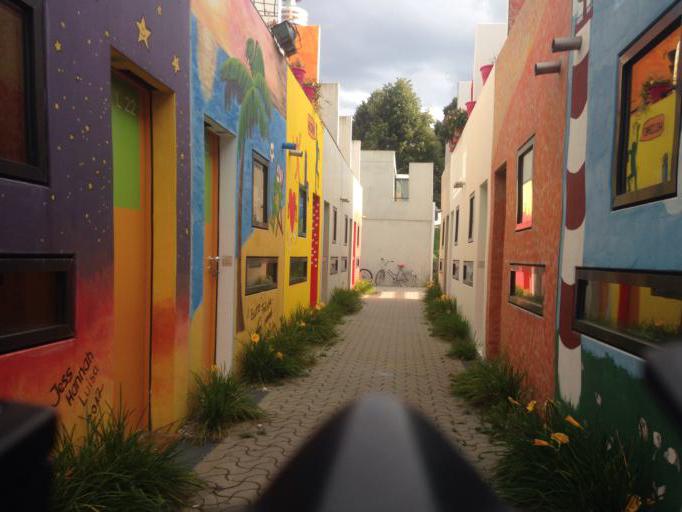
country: DE
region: Bavaria
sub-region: Upper Bavaria
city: Munich
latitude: 48.1791
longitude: 11.5525
